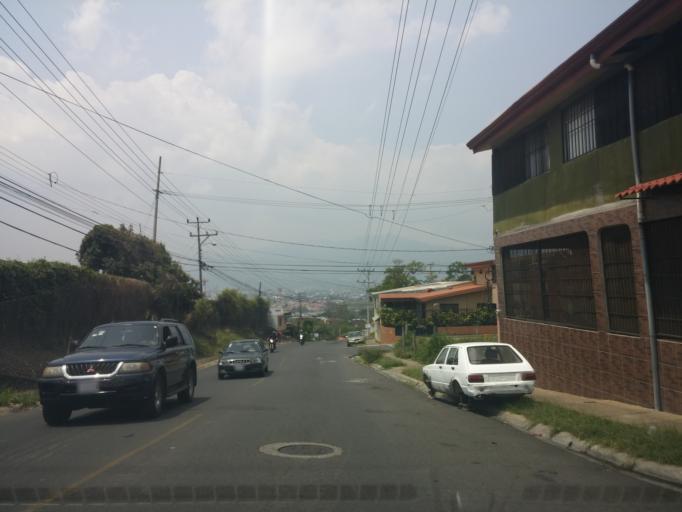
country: CR
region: Heredia
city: San Francisco
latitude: 9.9866
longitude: -84.1209
